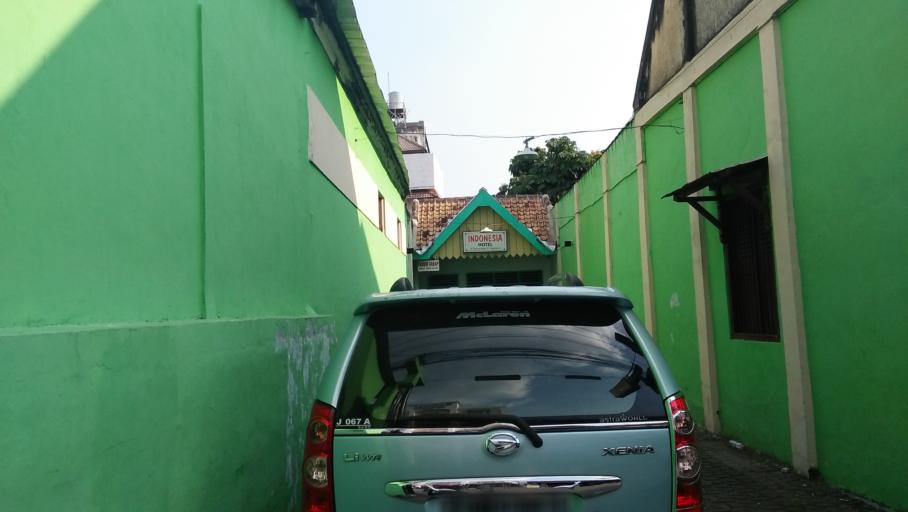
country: ID
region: Daerah Istimewa Yogyakarta
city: Yogyakarta
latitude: -7.7918
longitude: 110.3652
